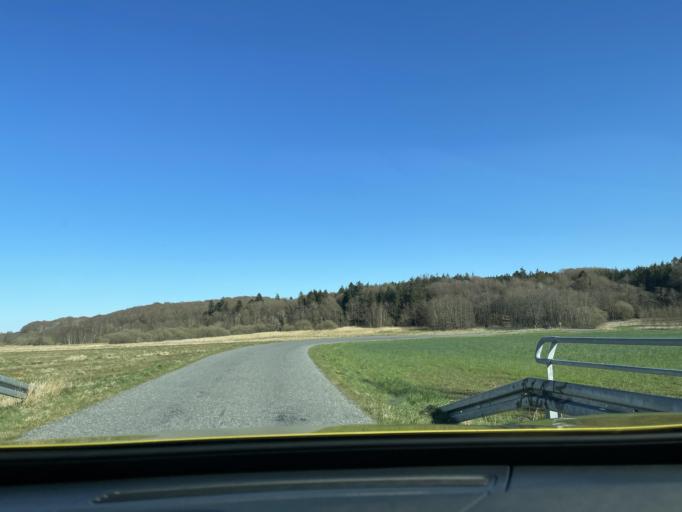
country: DK
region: Central Jutland
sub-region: Silkeborg Kommune
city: Kjellerup
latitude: 56.2477
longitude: 9.4674
